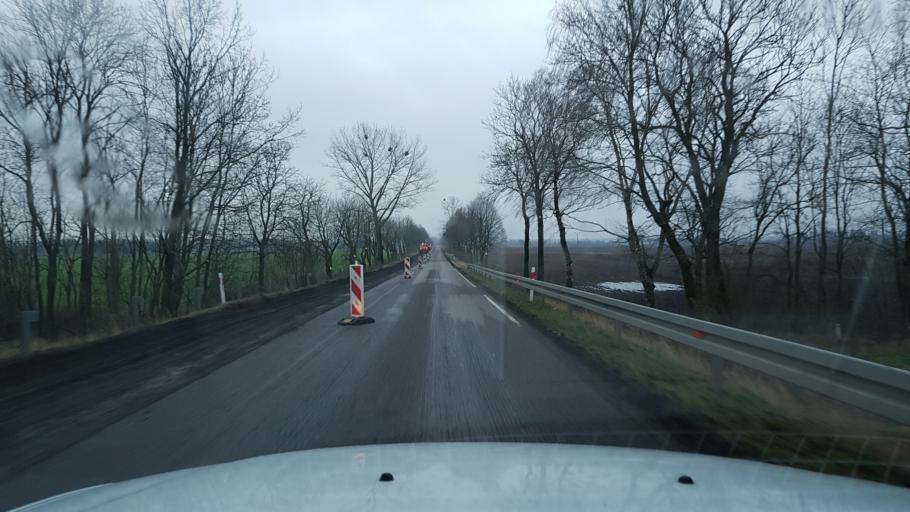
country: PL
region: West Pomeranian Voivodeship
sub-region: Powiat gryficki
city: Ploty
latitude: 53.8301
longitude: 15.2452
